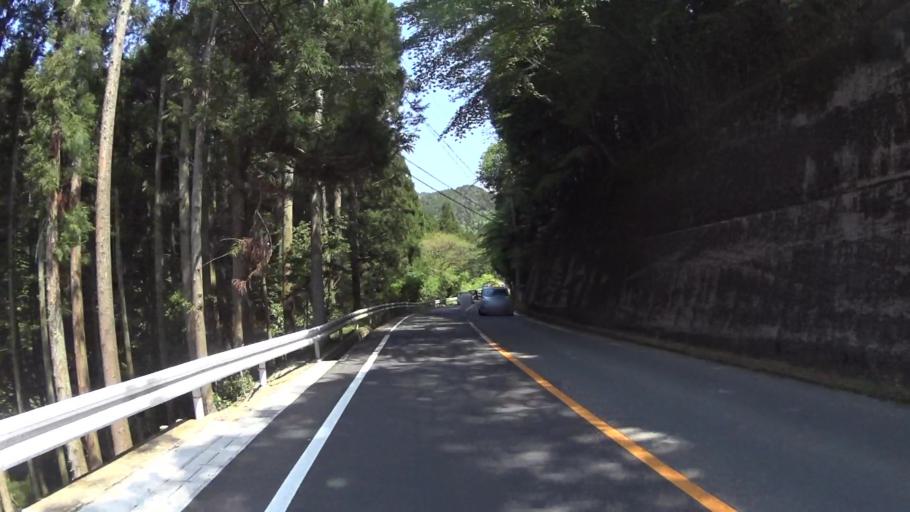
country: JP
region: Shiga Prefecture
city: Kitahama
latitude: 35.1370
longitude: 135.8357
